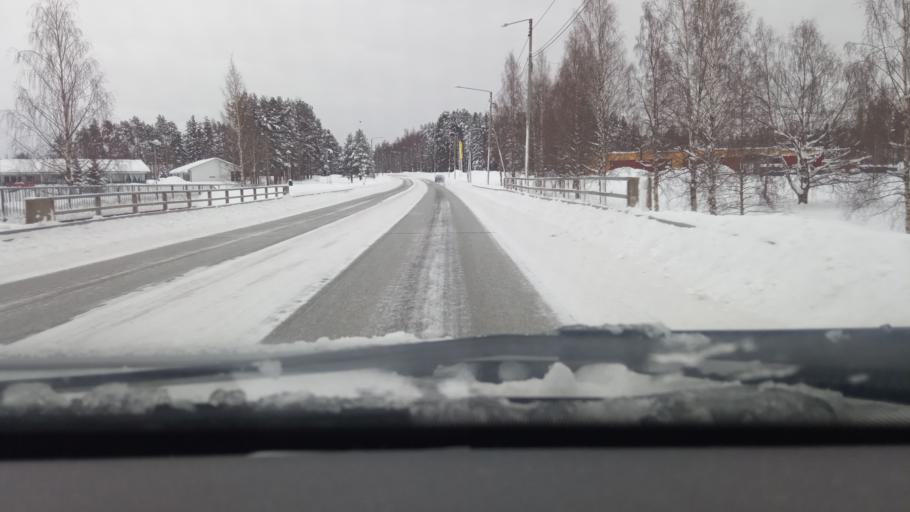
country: FI
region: Southern Ostrobothnia
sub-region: Jaerviseutu
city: Alajaervi
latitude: 62.9960
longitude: 23.8165
